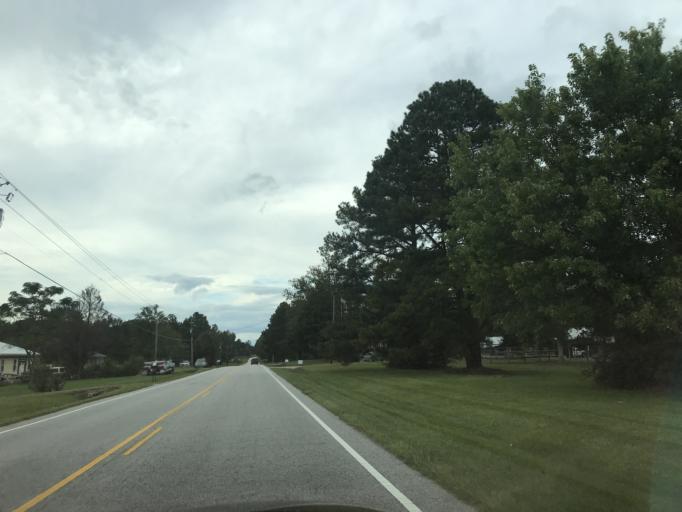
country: US
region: North Carolina
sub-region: Franklin County
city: Youngsville
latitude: 35.9921
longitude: -78.4071
